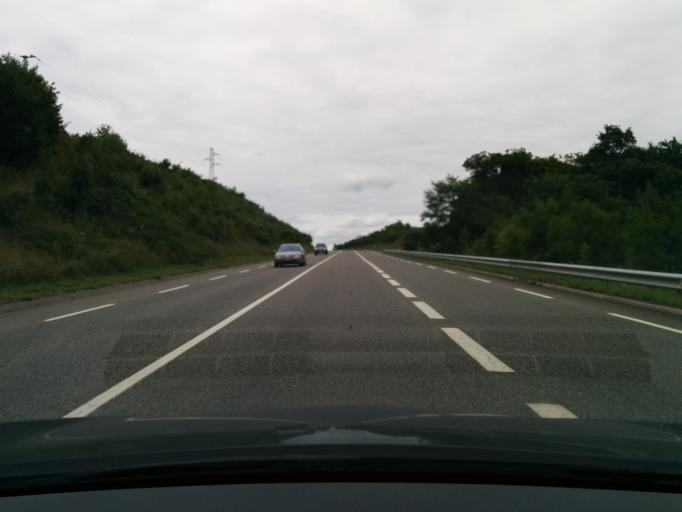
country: FR
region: Midi-Pyrenees
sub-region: Departement des Hautes-Pyrenees
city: La Barthe-de-Neste
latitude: 43.0331
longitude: 0.3665
